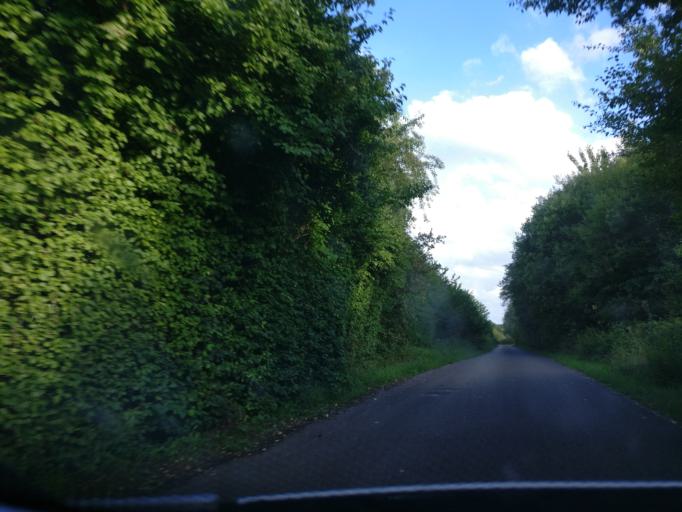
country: DE
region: Baden-Wuerttemberg
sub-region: Karlsruhe Region
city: Karlsruhe
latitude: 49.0159
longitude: 8.4707
